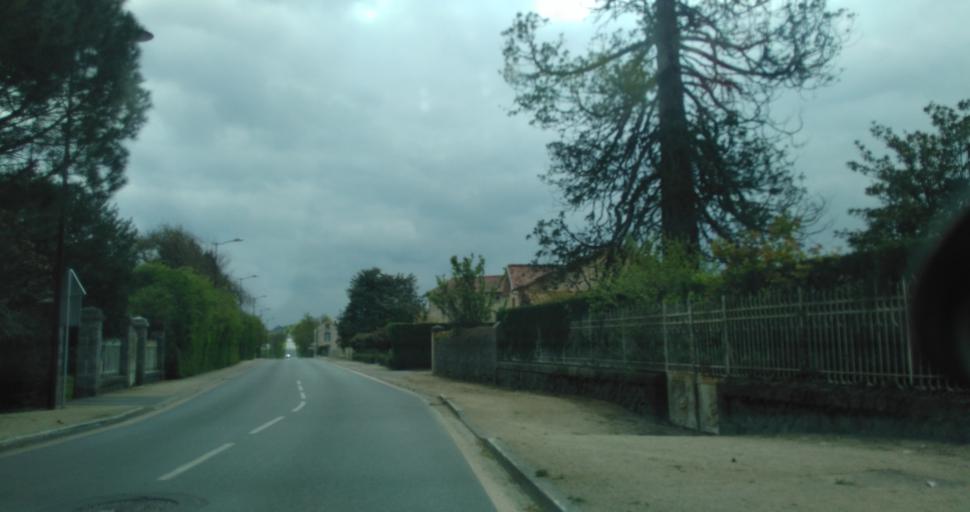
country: FR
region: Poitou-Charentes
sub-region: Departement des Deux-Sevres
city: Moncoutant
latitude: 46.7370
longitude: -0.6029
